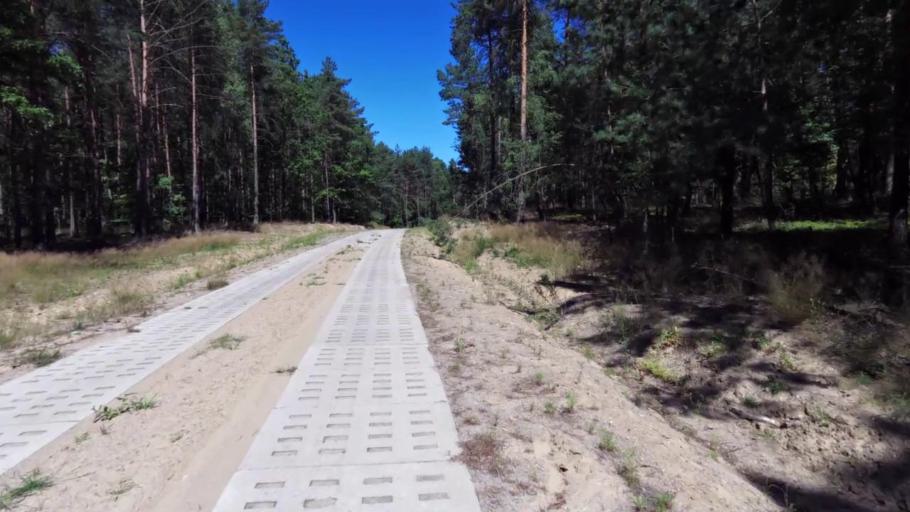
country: PL
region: West Pomeranian Voivodeship
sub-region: Powiat szczecinecki
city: Szczecinek
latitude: 53.6027
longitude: 16.6624
